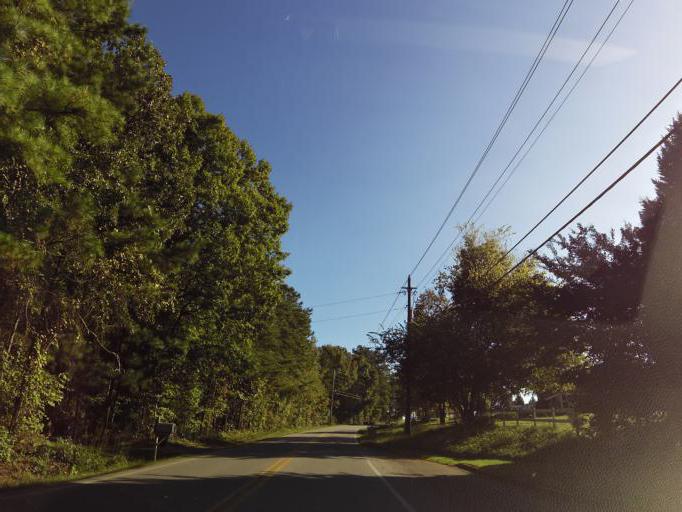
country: US
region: Georgia
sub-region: Cobb County
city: Acworth
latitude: 34.1219
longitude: -84.6800
